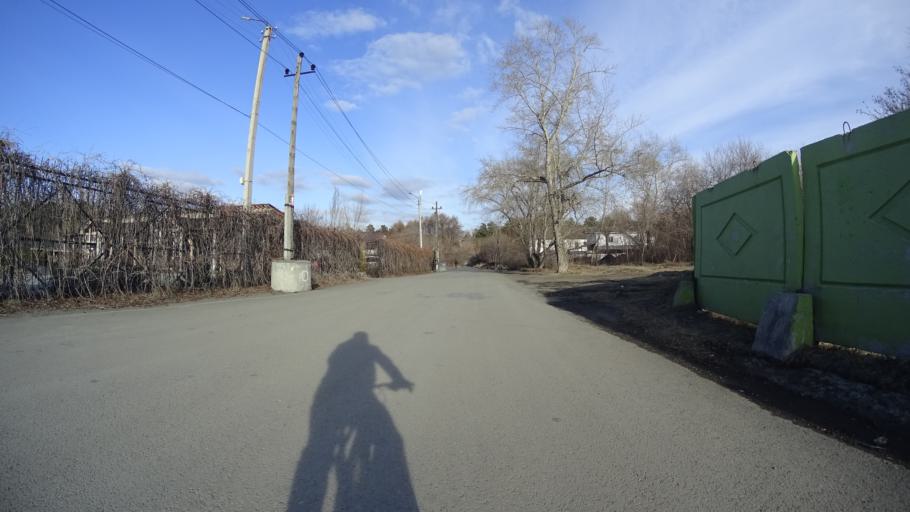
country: RU
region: Chelyabinsk
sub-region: Gorod Chelyabinsk
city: Chelyabinsk
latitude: 55.1291
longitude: 61.3618
